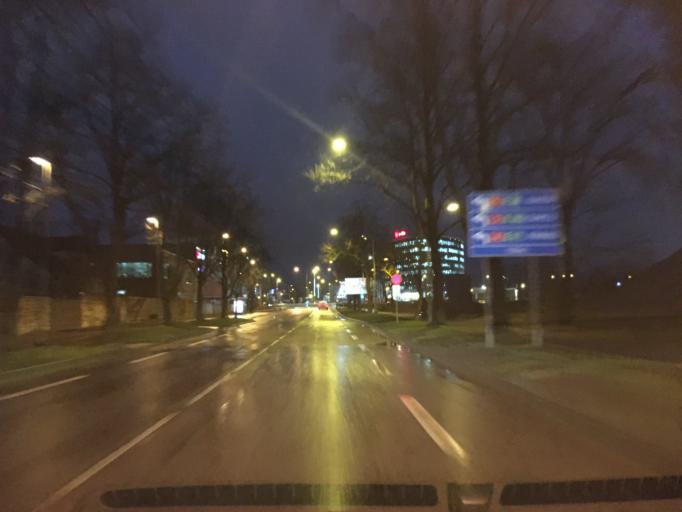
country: EE
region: Harju
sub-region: Tallinna linn
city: Tallinn
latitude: 59.4204
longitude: 24.7510
